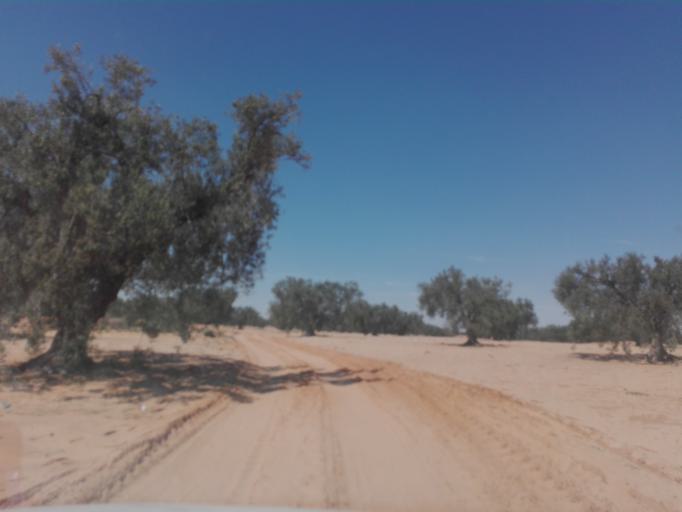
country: TN
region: Safaqis
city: Bi'r `Ali Bin Khalifah
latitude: 34.6624
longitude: 10.3173
